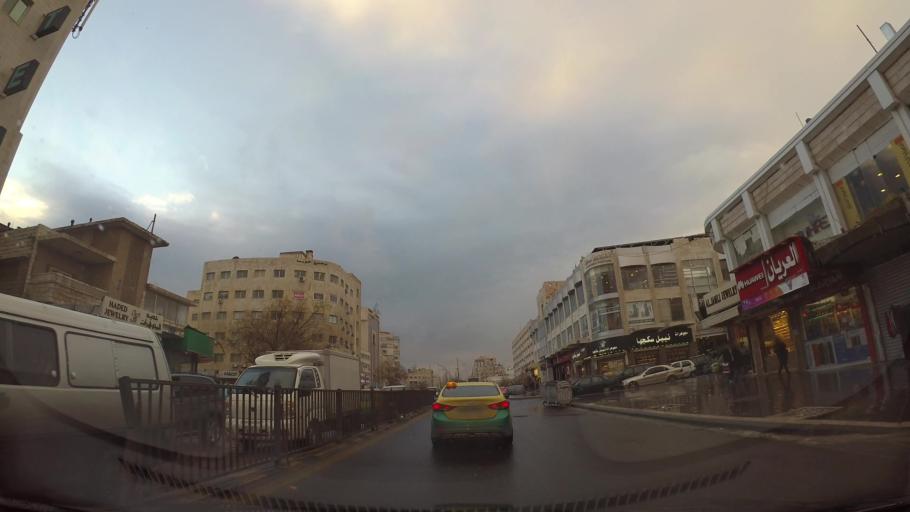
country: JO
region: Amman
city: Amman
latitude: 31.9689
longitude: 35.9159
